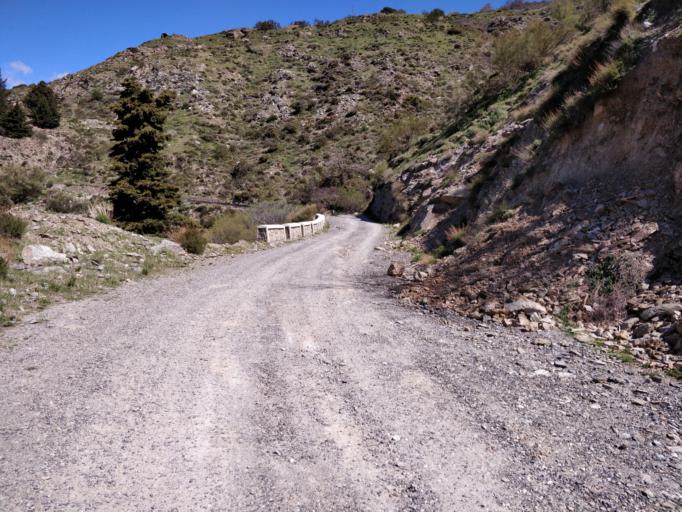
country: ES
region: Andalusia
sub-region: Provincia de Granada
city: Soportujar
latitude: 36.9331
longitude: -3.4001
